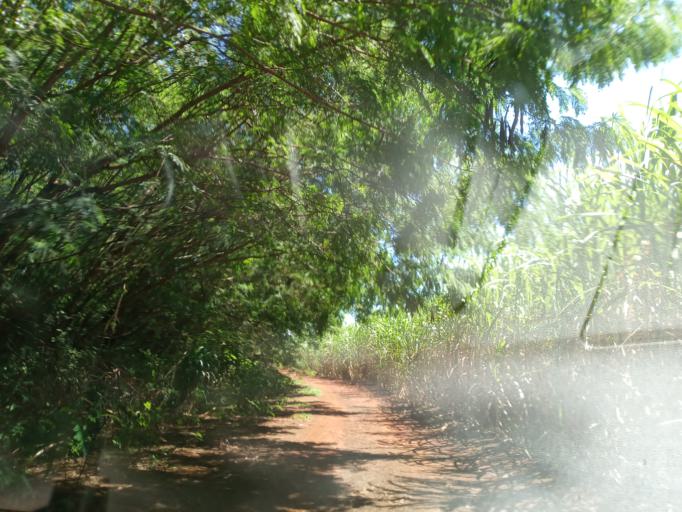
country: BR
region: Goias
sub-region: Itumbiara
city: Itumbiara
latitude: -18.4424
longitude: -49.1418
